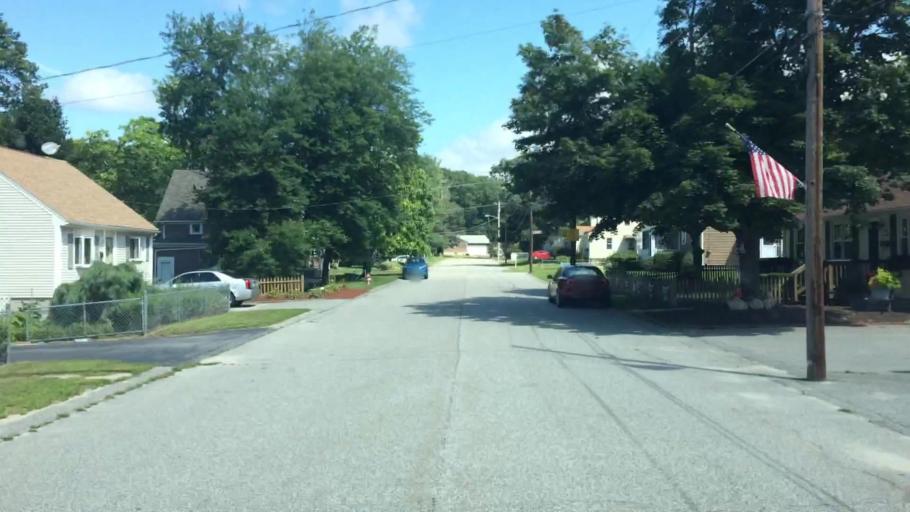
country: US
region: Rhode Island
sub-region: Providence County
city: Cumberland Hill
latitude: 41.9867
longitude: -71.4842
